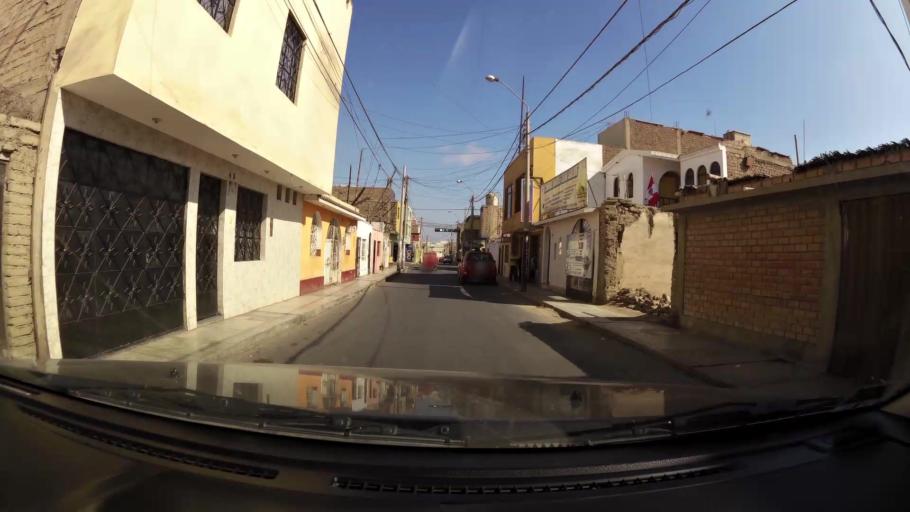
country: PE
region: Ica
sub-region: Provincia de Chincha
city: Chincha Alta
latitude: -13.4210
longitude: -76.1319
